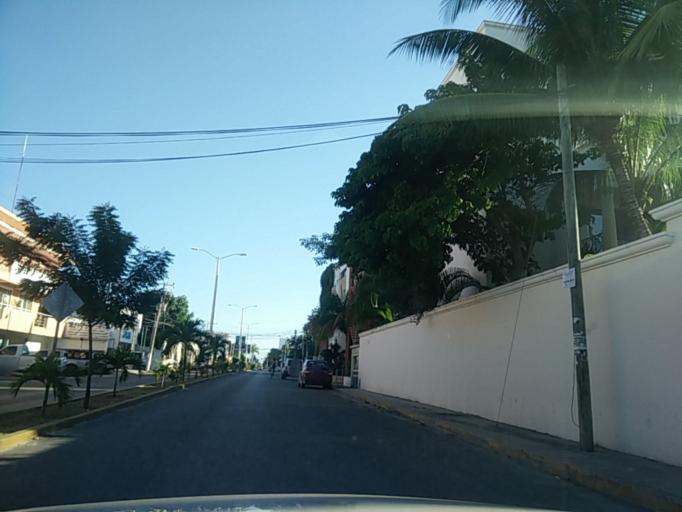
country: MX
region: Quintana Roo
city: Playa del Carmen
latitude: 20.6361
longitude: -87.0670
